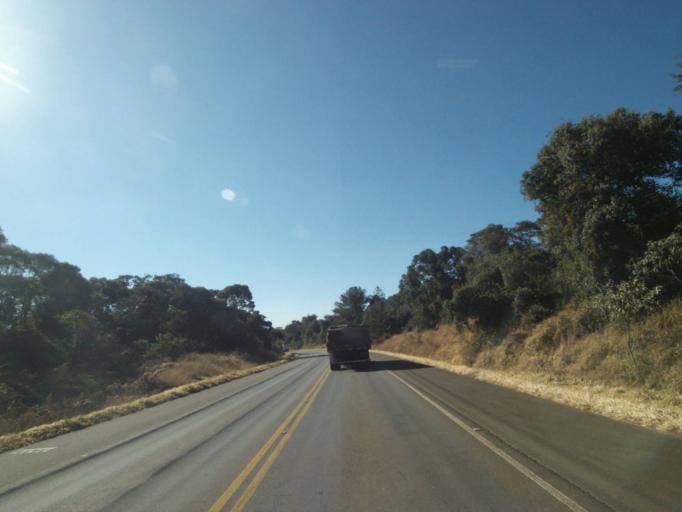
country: BR
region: Parana
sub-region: Tibagi
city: Tibagi
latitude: -24.6657
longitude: -50.4521
